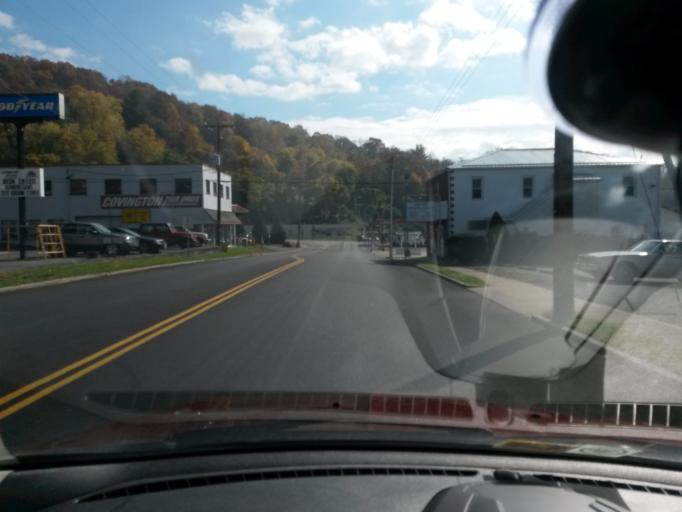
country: US
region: Virginia
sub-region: City of Covington
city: Fairlawn
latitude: 37.7836
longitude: -79.9863
